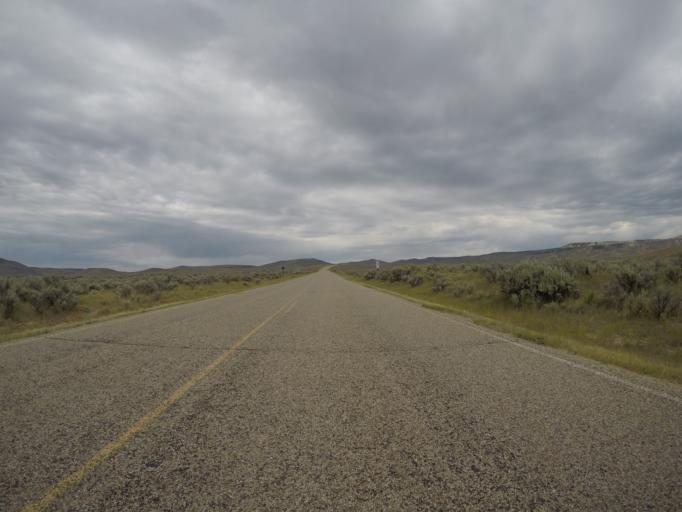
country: US
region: Wyoming
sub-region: Lincoln County
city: Kemmerer
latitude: 41.8251
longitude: -110.7641
